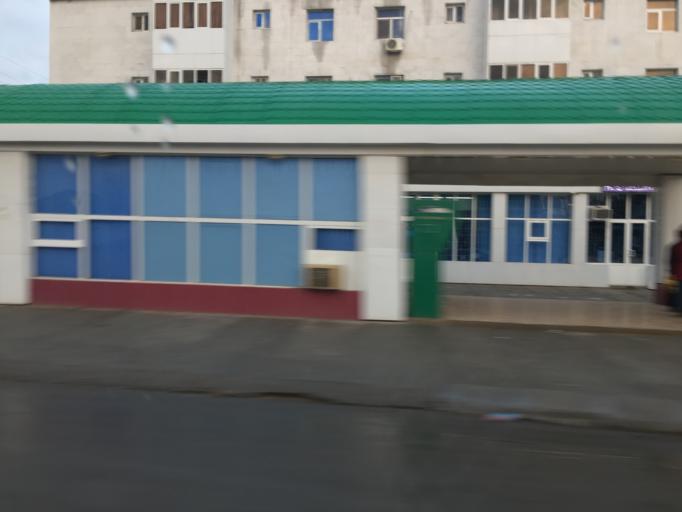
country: TM
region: Mary
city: Mary
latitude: 37.5866
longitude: 61.8383
